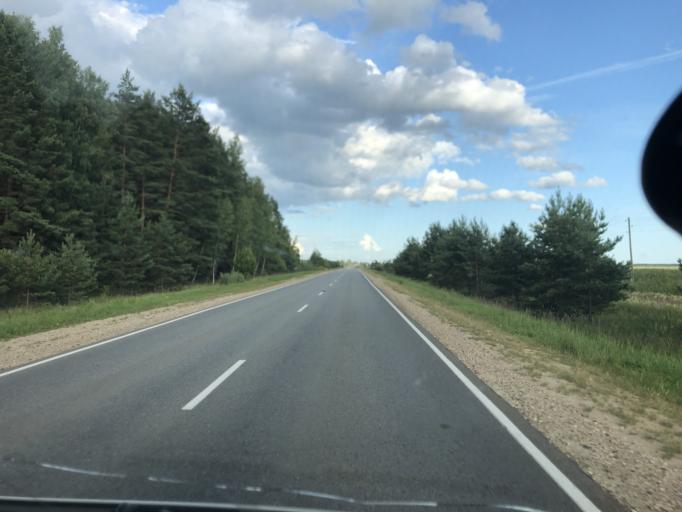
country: RU
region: Kaluga
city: Yukhnov
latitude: 54.7093
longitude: 35.2574
